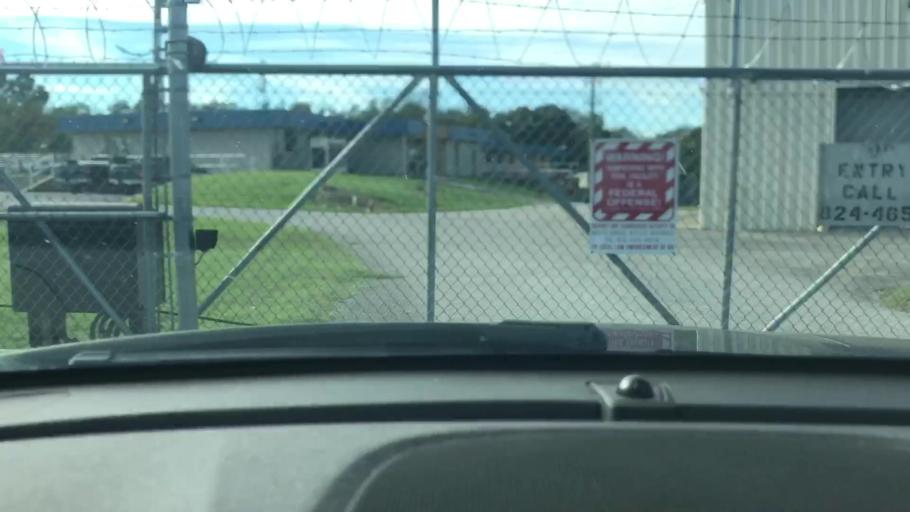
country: US
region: Tennessee
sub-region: Sumner County
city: Hendersonville
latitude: 36.3023
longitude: -86.6510
